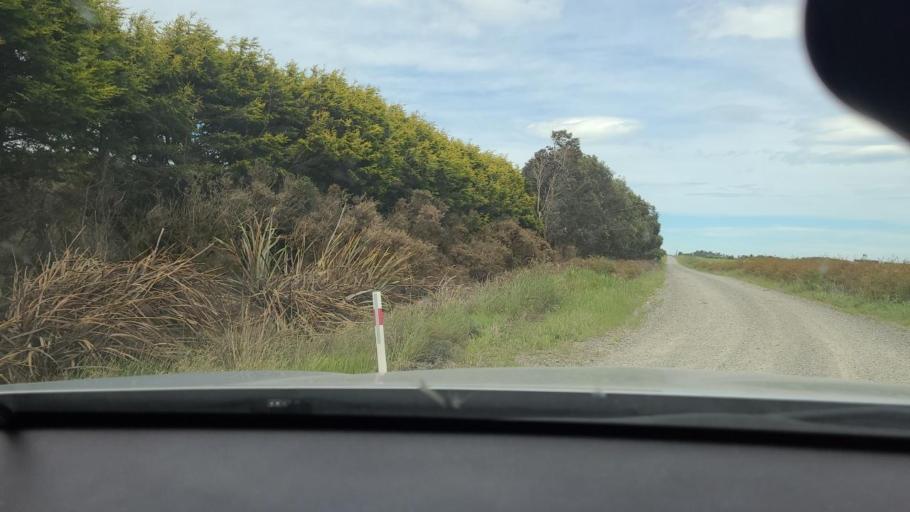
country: NZ
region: Southland
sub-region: Southland District
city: Riverton
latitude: -46.3457
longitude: 168.1824
